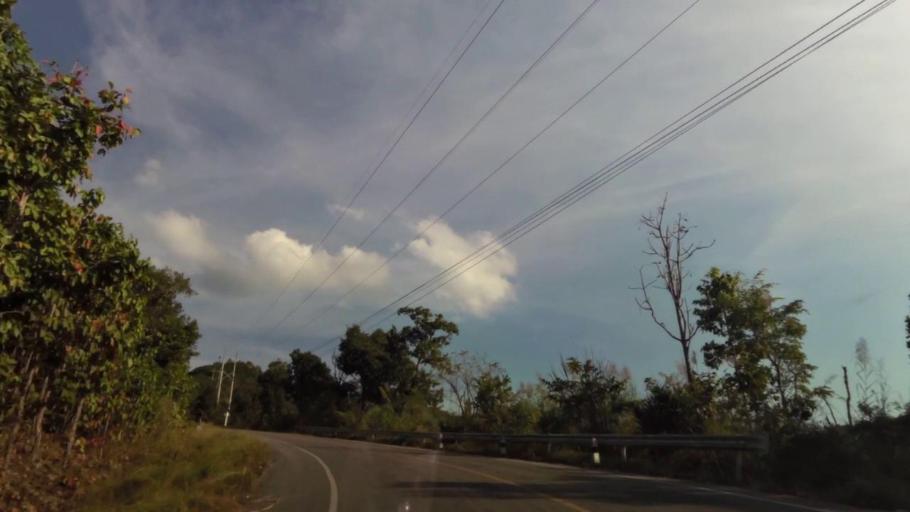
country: TH
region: Chiang Rai
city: Khun Tan
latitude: 19.8787
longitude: 100.3103
